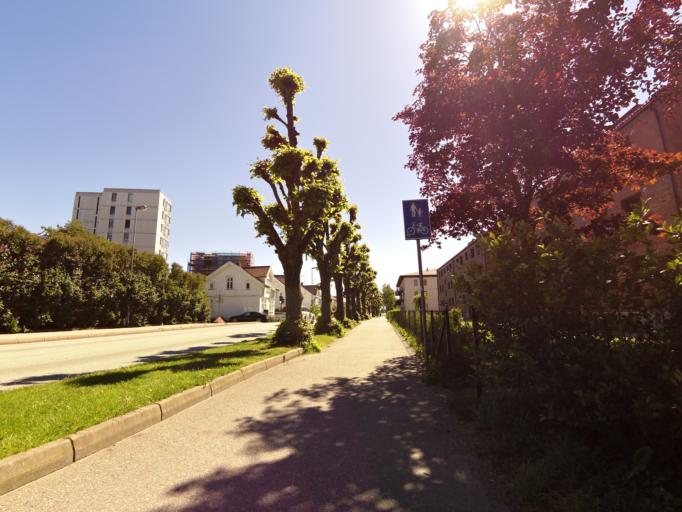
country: NO
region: Vest-Agder
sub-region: Kristiansand
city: Kristiansand
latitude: 58.1576
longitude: 8.0116
